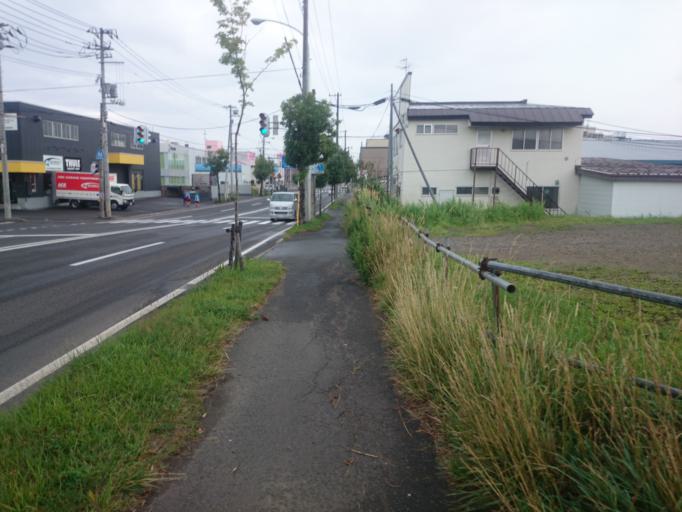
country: JP
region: Hokkaido
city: Sapporo
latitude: 43.0578
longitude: 141.4010
